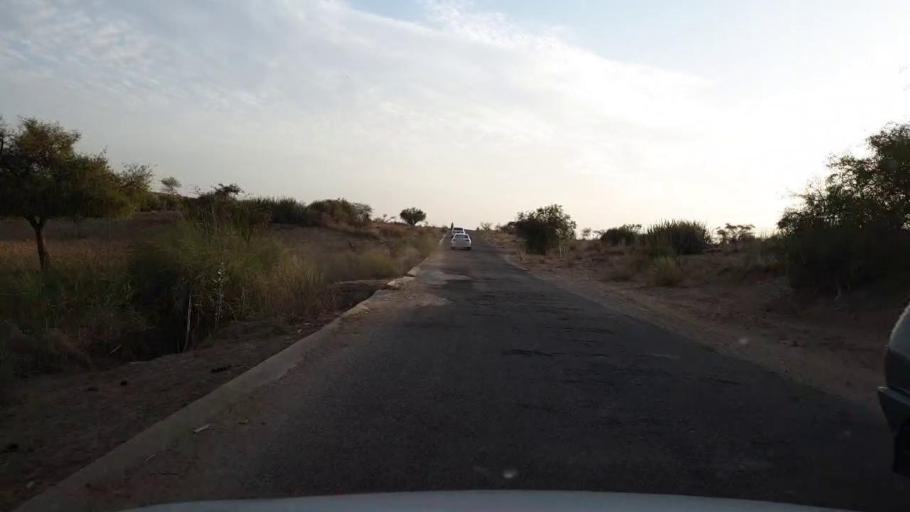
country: PK
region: Sindh
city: Nabisar
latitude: 25.0138
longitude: 69.9376
